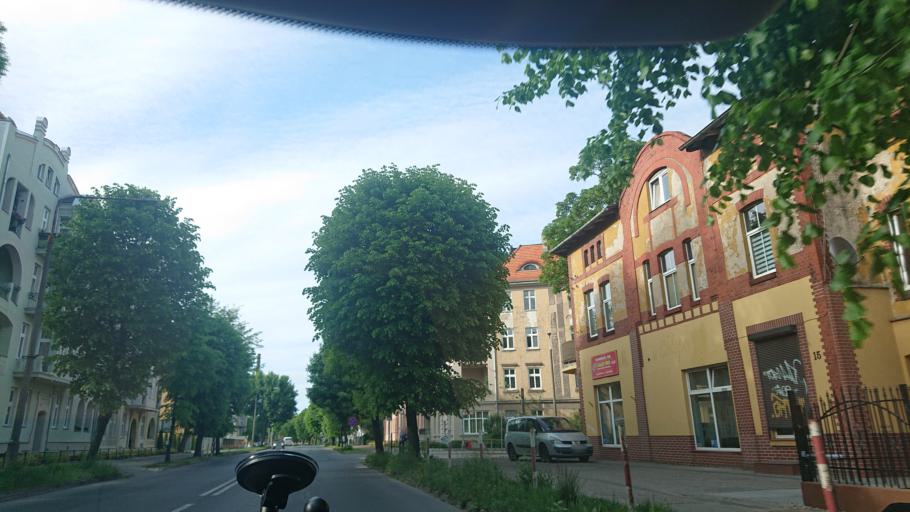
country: PL
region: Greater Poland Voivodeship
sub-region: Powiat gnieznienski
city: Gniezno
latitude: 52.5245
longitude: 17.5972
